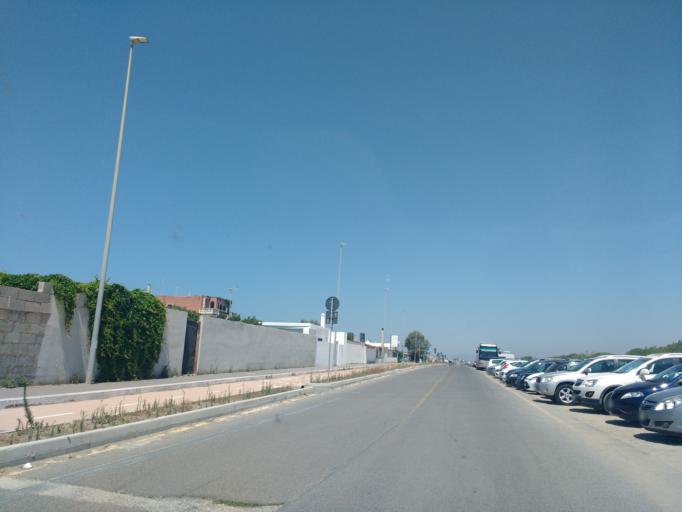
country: IT
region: Latium
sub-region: Citta metropolitana di Roma Capitale
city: Fregene
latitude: 41.8747
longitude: 12.1790
